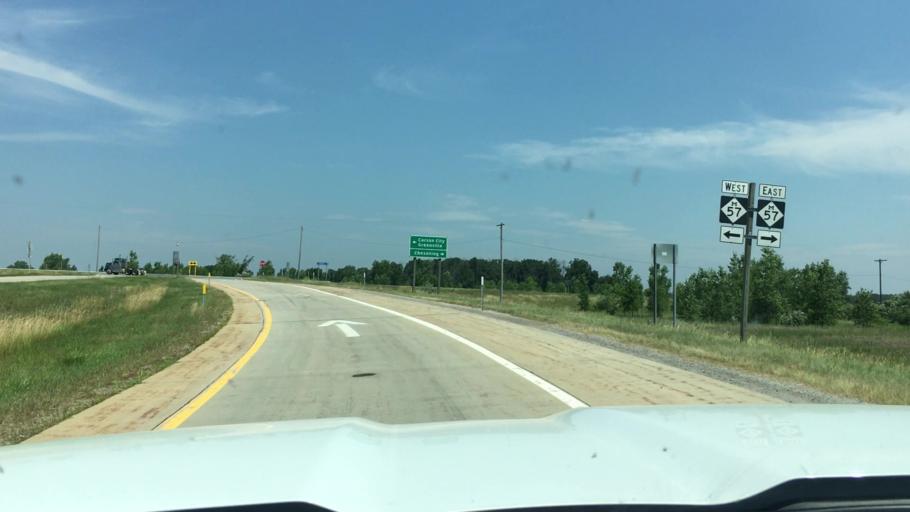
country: US
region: Michigan
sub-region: Gratiot County
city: Ithaca
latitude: 43.1745
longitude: -84.5612
